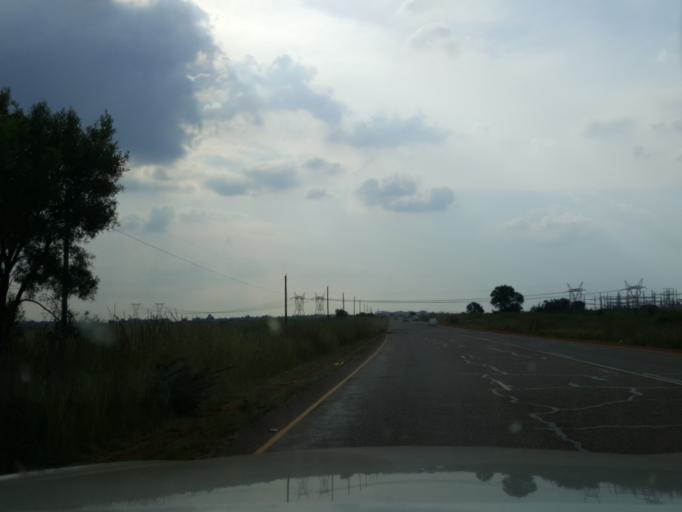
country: ZA
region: Gauteng
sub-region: City of Tshwane Metropolitan Municipality
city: Centurion
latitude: -25.8540
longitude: 28.2950
